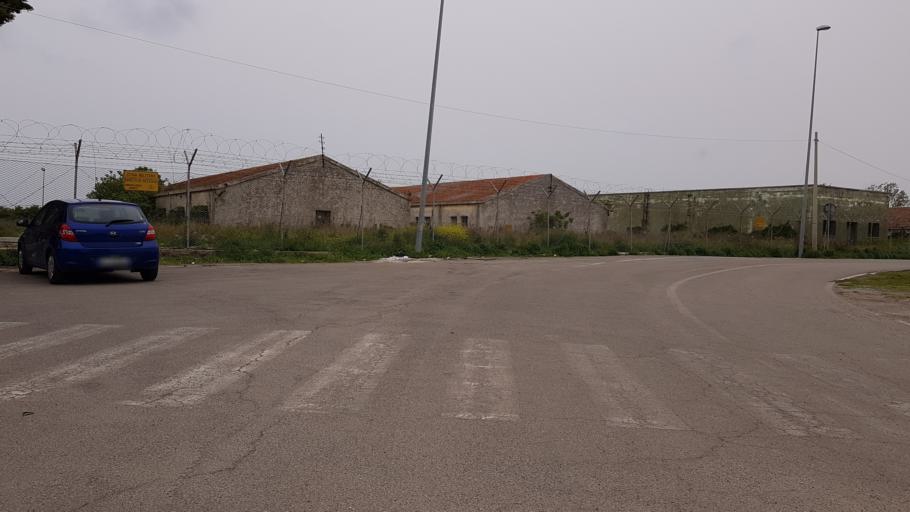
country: IT
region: Apulia
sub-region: Provincia di Brindisi
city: Brindisi
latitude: 40.6542
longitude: 17.9348
